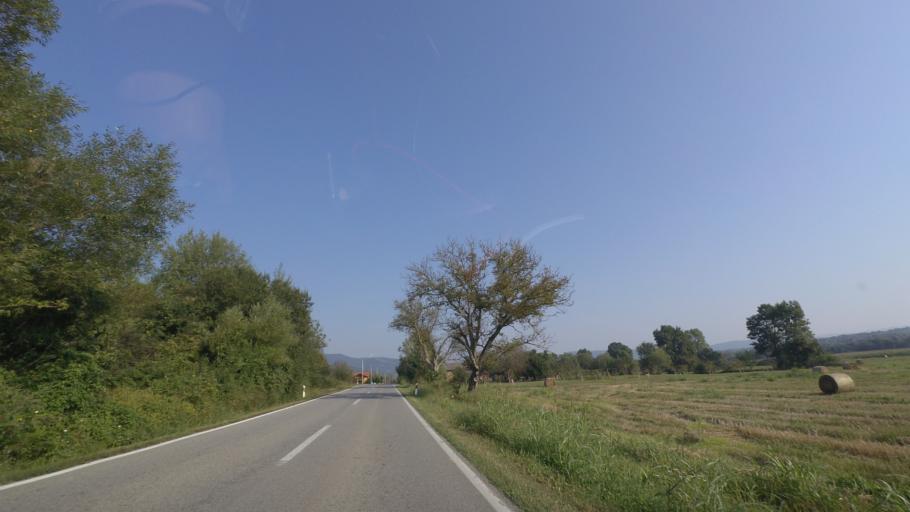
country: HR
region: Brodsko-Posavska
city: Resetari
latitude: 45.3820
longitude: 17.5123
